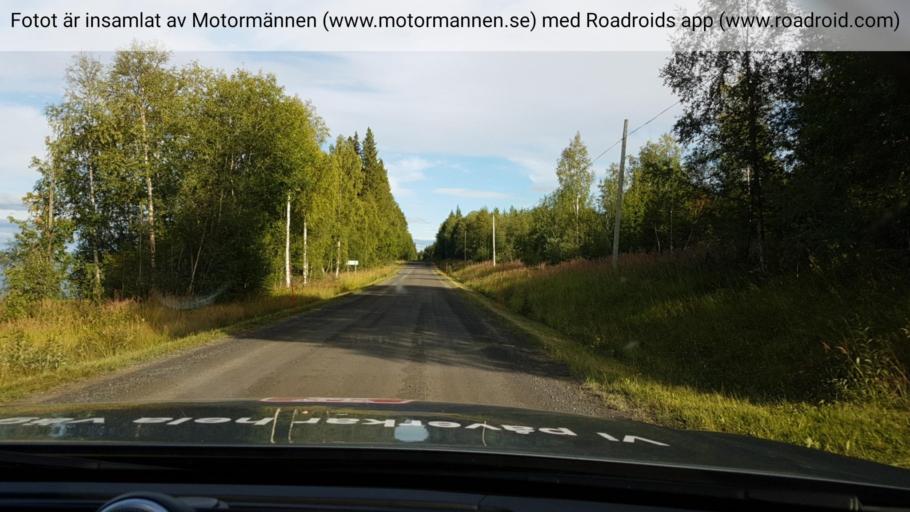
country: SE
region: Jaemtland
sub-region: Stroemsunds Kommun
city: Stroemsund
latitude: 64.1412
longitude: 15.7357
